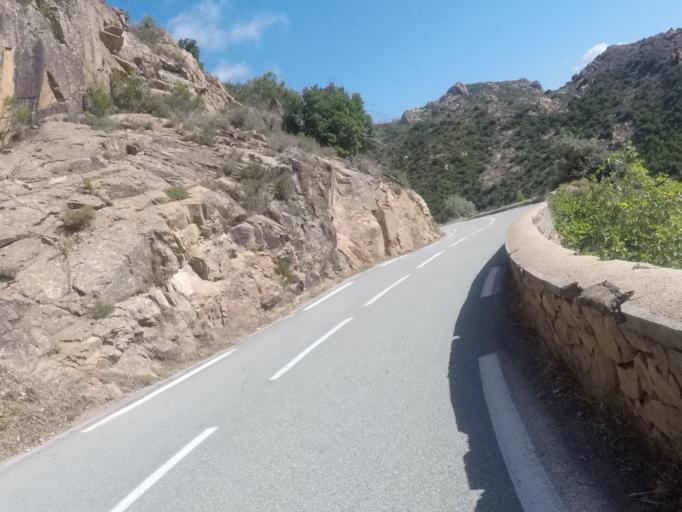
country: FR
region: Corsica
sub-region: Departement de la Corse-du-Sud
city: Grosseto-Prugna
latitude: 41.7692
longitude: 9.0434
